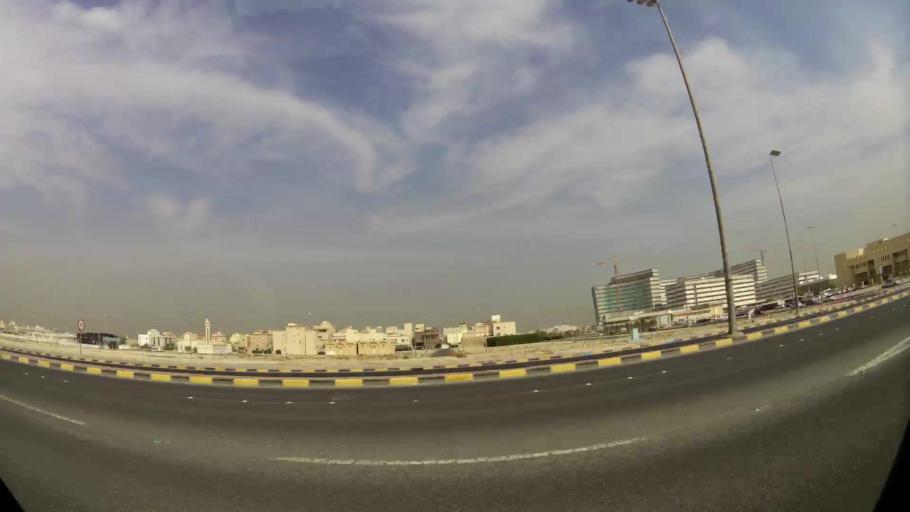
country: KW
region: Al Farwaniyah
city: Janub as Surrah
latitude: 29.2715
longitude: 48.0121
